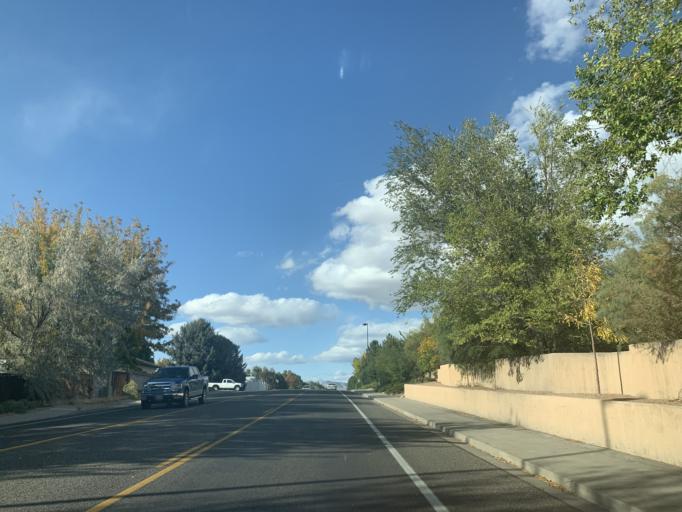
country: US
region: Colorado
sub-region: Mesa County
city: Grand Junction
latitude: 39.0996
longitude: -108.5430
